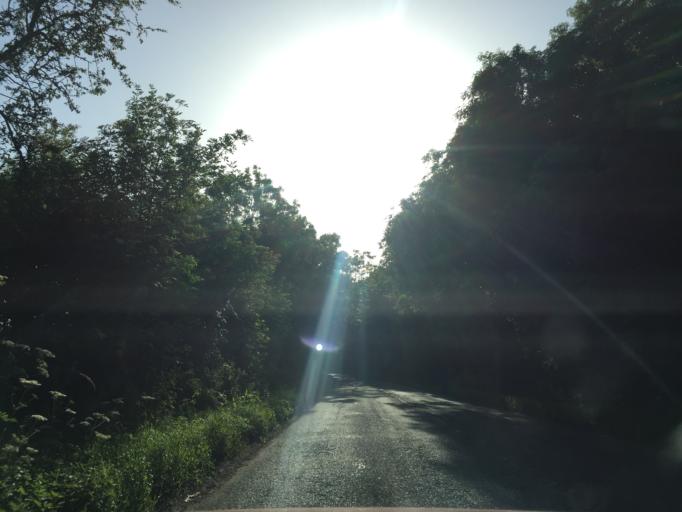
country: GB
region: England
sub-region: Gloucestershire
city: Cirencester
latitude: 51.7188
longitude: -1.9320
